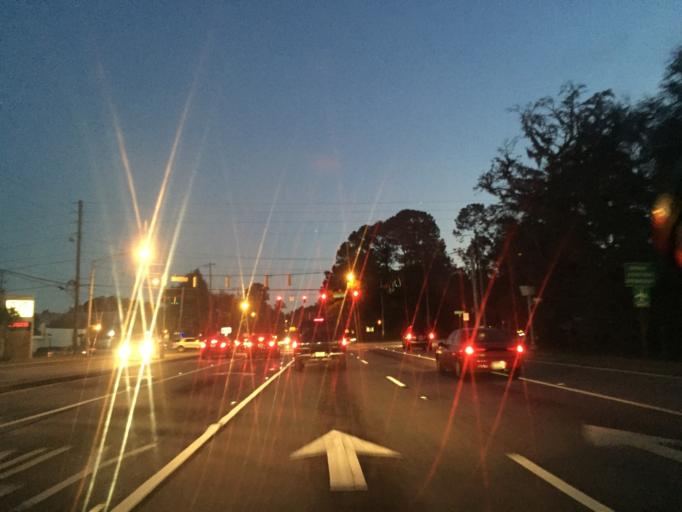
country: US
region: Georgia
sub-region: Chatham County
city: Savannah
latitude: 32.0275
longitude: -81.1083
